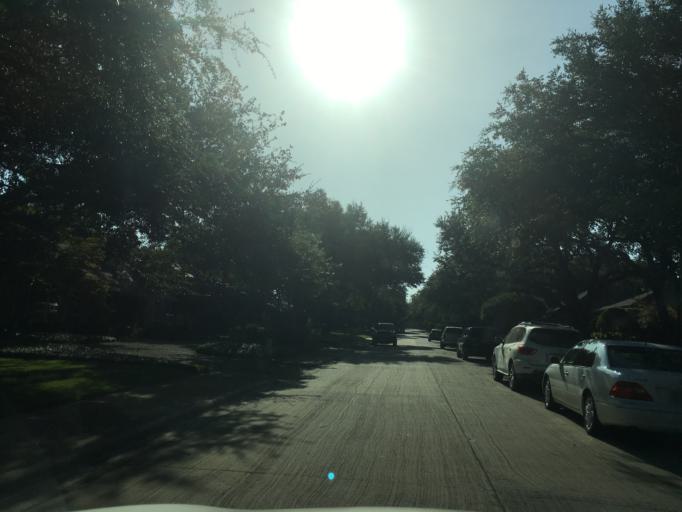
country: US
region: Texas
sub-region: Dallas County
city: Richardson
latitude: 32.8905
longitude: -96.7233
